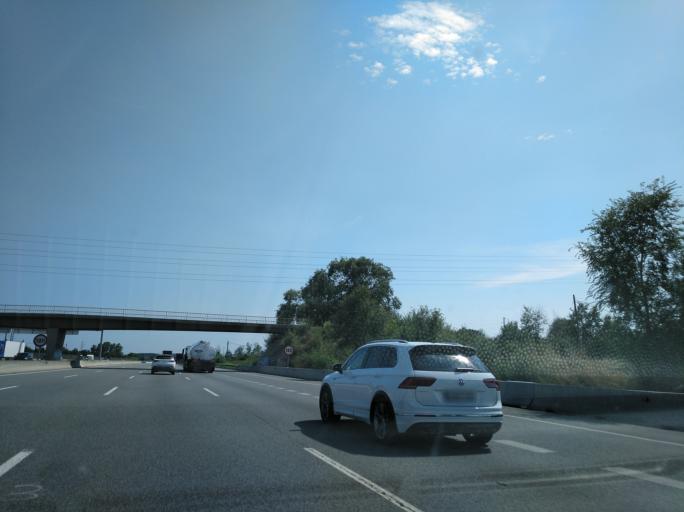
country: ES
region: Catalonia
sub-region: Provincia de Girona
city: Vilablareix
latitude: 41.9562
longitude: 2.7852
